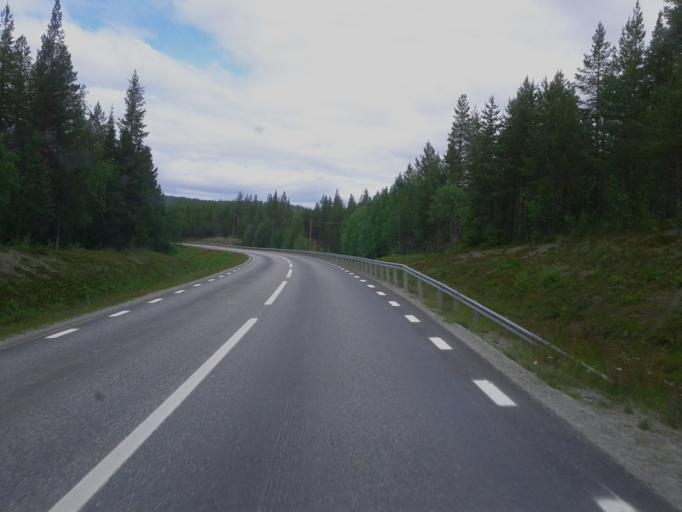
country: SE
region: Vaesterbotten
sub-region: Storumans Kommun
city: Fristad
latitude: 65.3801
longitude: 16.5132
